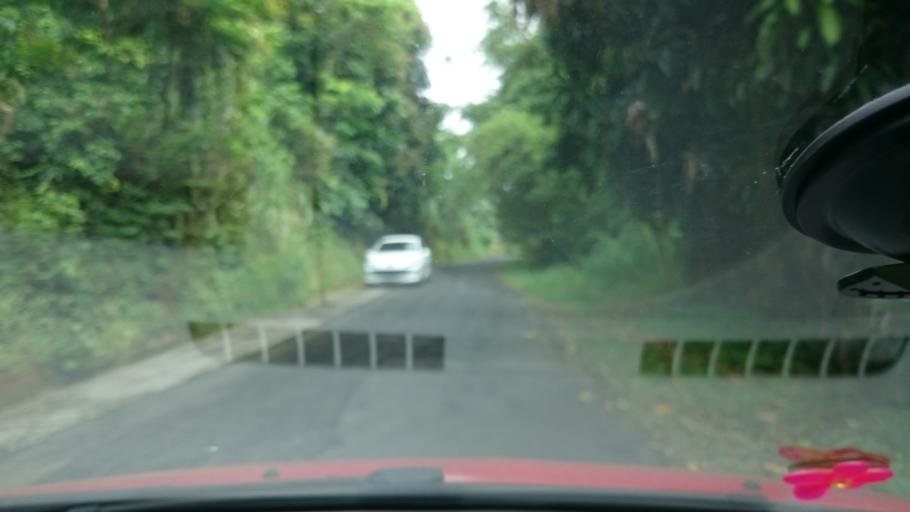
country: MQ
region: Martinique
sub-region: Martinique
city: Riviere-Pilote
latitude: 14.4928
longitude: -60.9105
